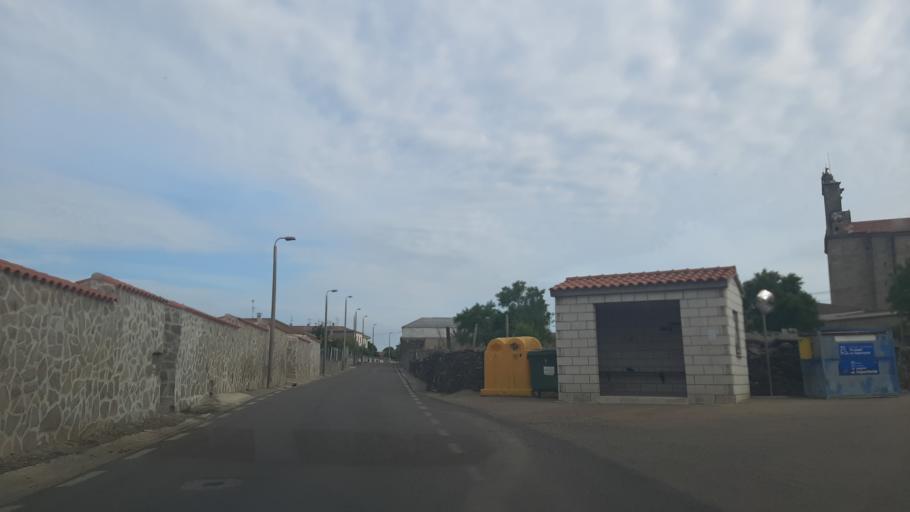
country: ES
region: Castille and Leon
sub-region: Provincia de Salamanca
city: Gallegos de Arganan
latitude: 40.6299
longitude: -6.7038
